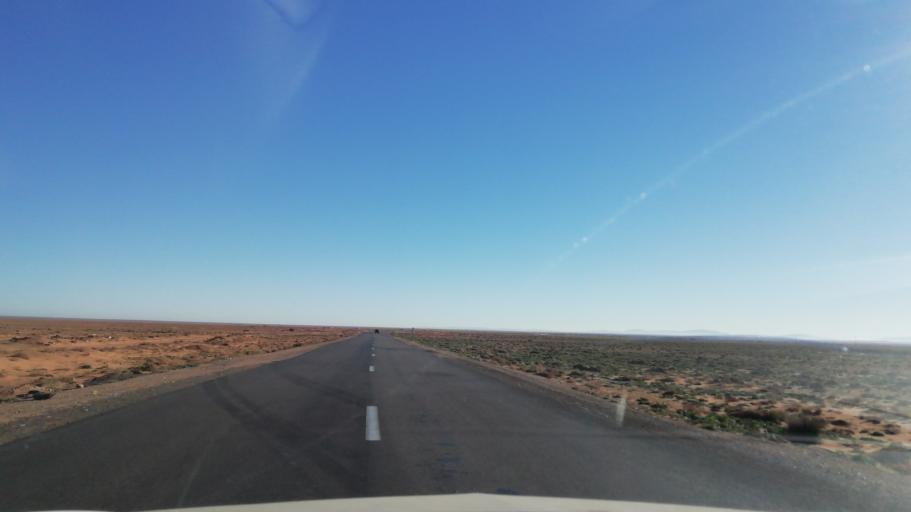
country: DZ
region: El Bayadh
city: El Bayadh
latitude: 33.8596
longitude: 0.5490
